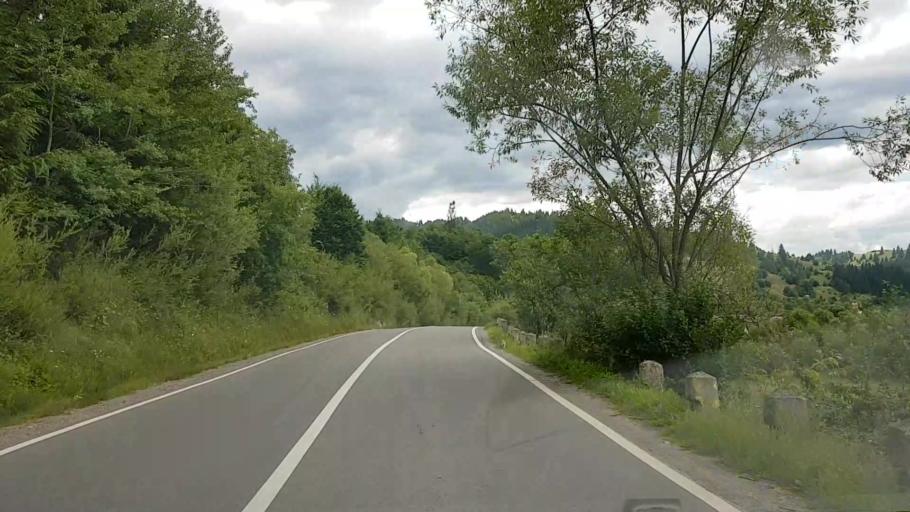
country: RO
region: Neamt
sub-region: Comuna Farcasa
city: Farcasa
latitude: 47.1594
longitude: 25.8264
